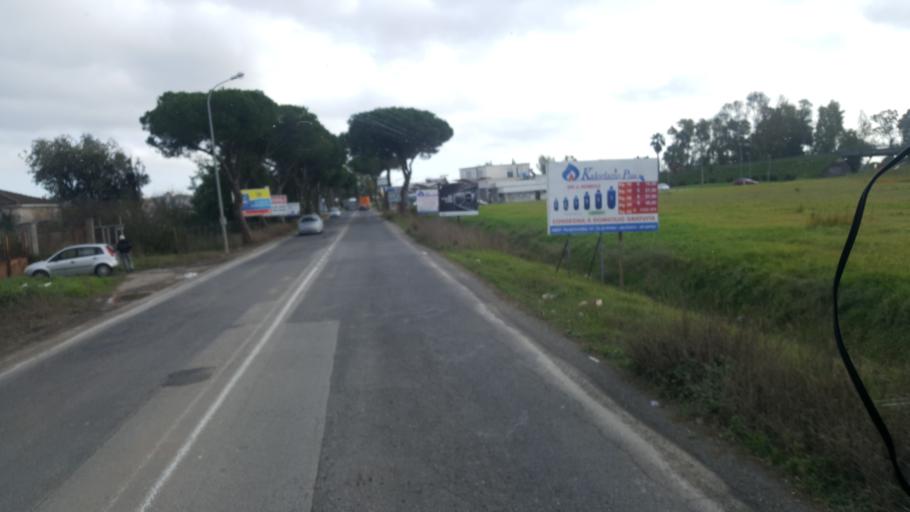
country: IT
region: Latium
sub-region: Provincia di Latina
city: Borgo Podgora
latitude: 41.4829
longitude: 12.8612
